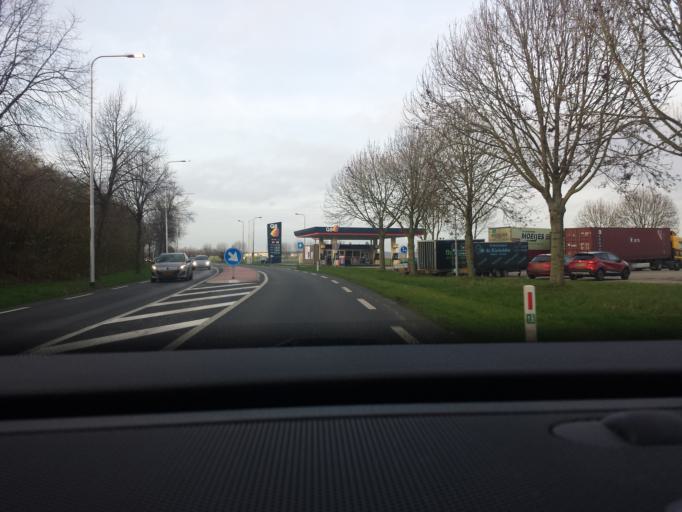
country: NL
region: Gelderland
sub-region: Gemeente Duiven
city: Duiven
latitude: 51.9525
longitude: 6.0363
